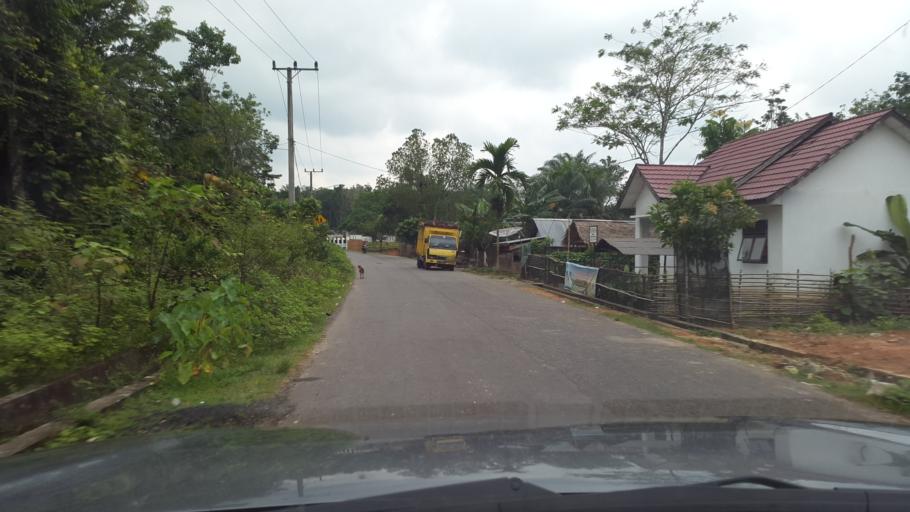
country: ID
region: South Sumatra
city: Gunungmenang
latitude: -3.1128
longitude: 103.9447
